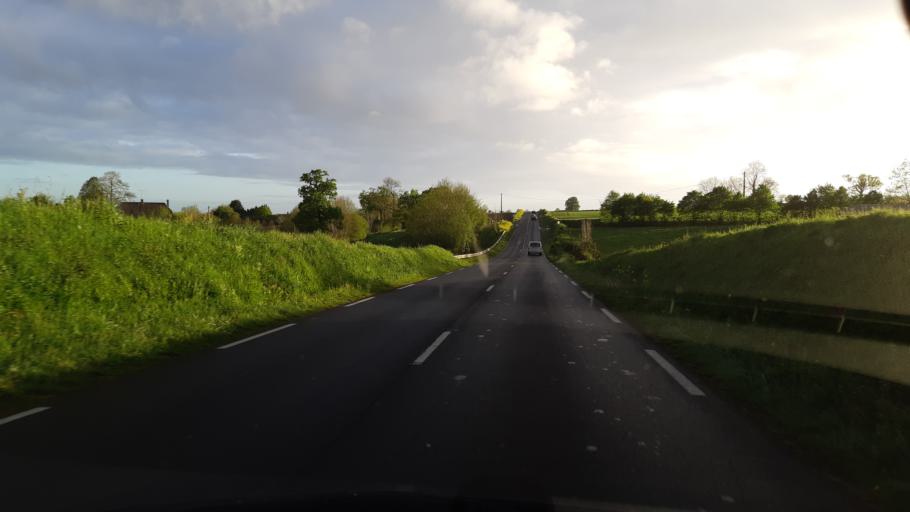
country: FR
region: Lower Normandy
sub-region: Departement de la Manche
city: Agneaux
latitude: 49.0353
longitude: -1.1340
